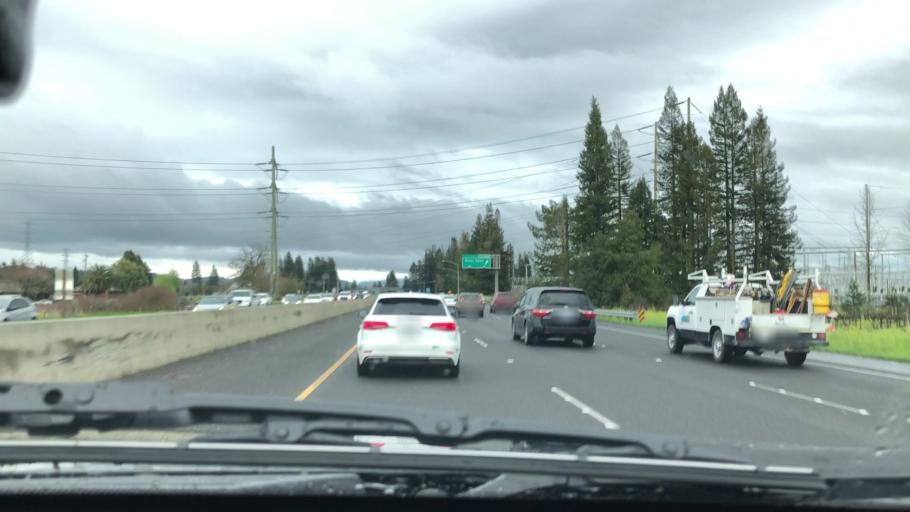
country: US
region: California
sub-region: Sonoma County
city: Larkfield-Wikiup
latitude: 38.4998
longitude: -122.7624
